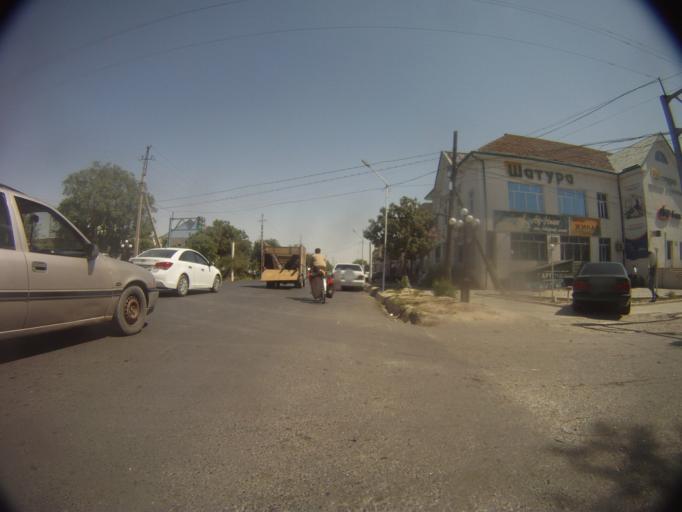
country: KZ
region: Ongtustik Qazaqstan
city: Turkestan
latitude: 43.3011
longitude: 68.2618
